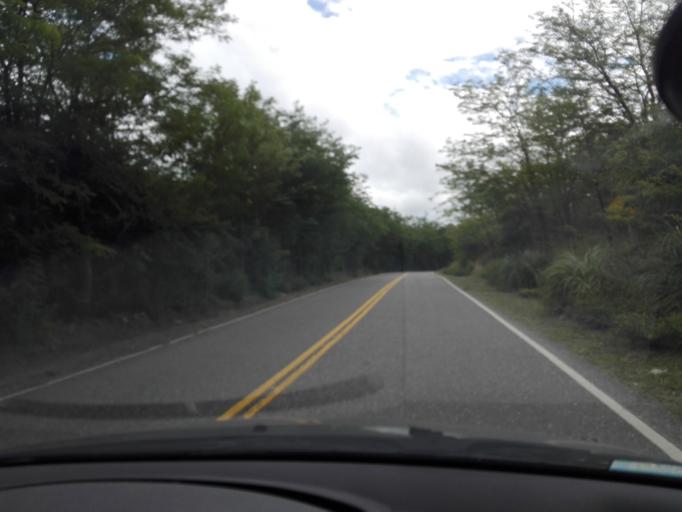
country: AR
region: Cordoba
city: Cuesta Blanca
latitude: -31.5920
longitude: -64.5689
